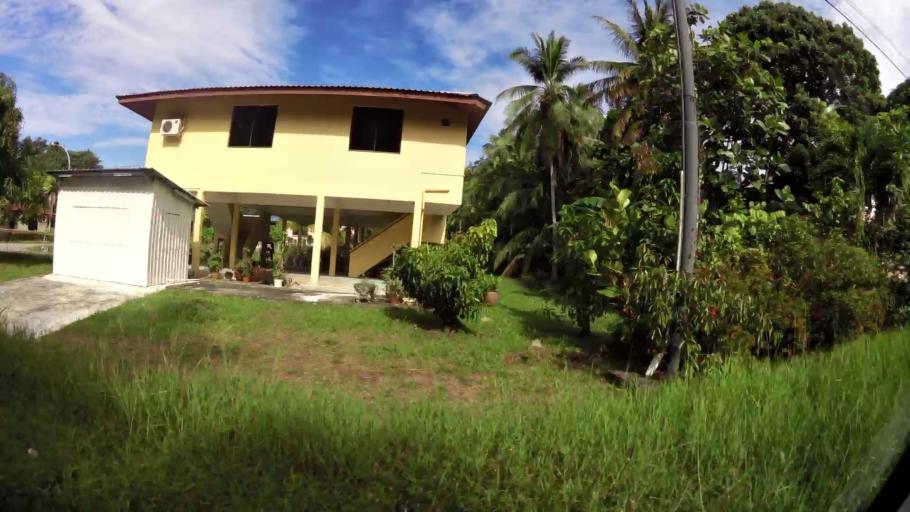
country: BN
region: Brunei and Muara
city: Bandar Seri Begawan
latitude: 4.9181
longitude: 114.8970
